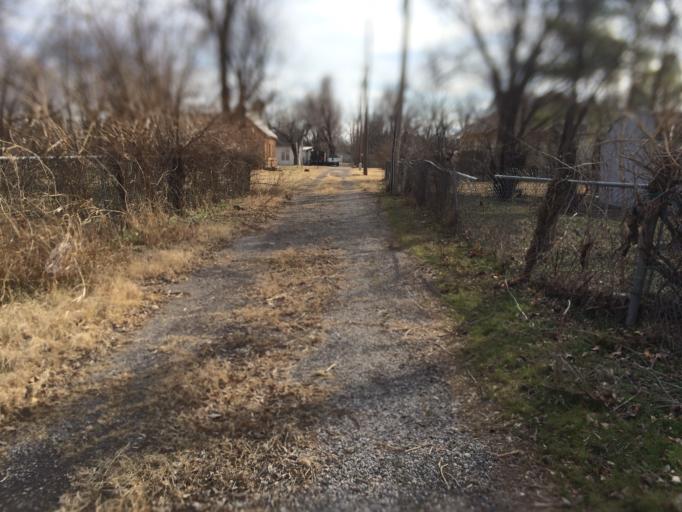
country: US
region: Oklahoma
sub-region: Cleveland County
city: Norman
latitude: 35.2275
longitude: -97.4335
